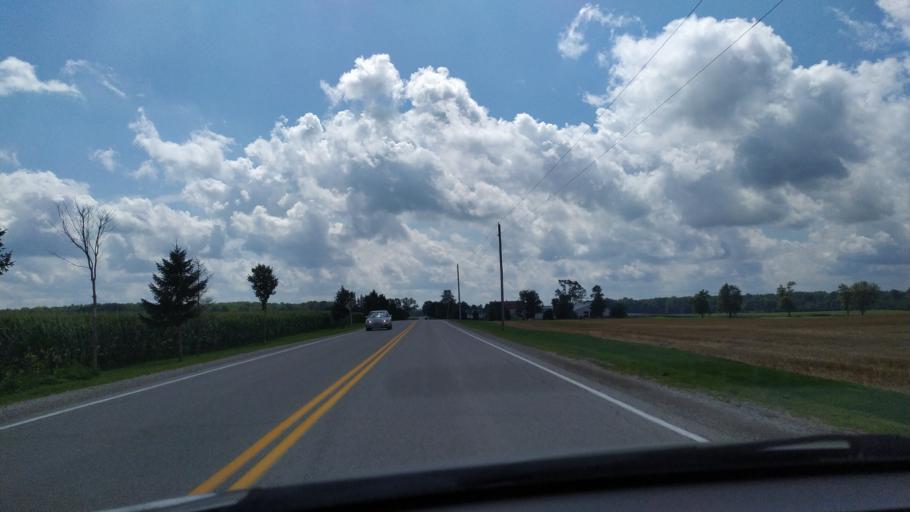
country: CA
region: Ontario
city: London
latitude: 43.0696
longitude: -81.3367
